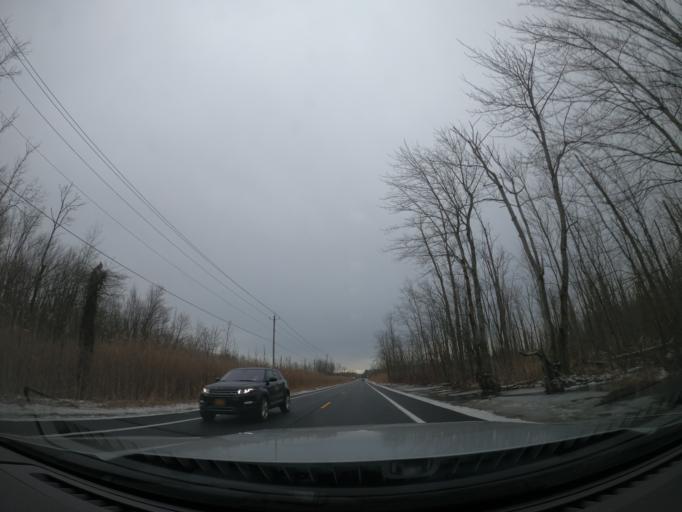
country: US
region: New York
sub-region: Madison County
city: Bridgeport
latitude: 43.1263
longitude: -75.9948
